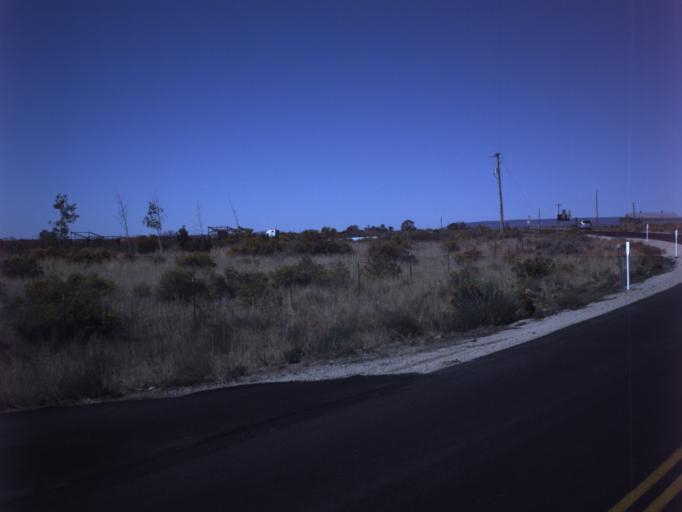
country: US
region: Utah
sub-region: San Juan County
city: Blanding
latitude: 37.5734
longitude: -109.4883
